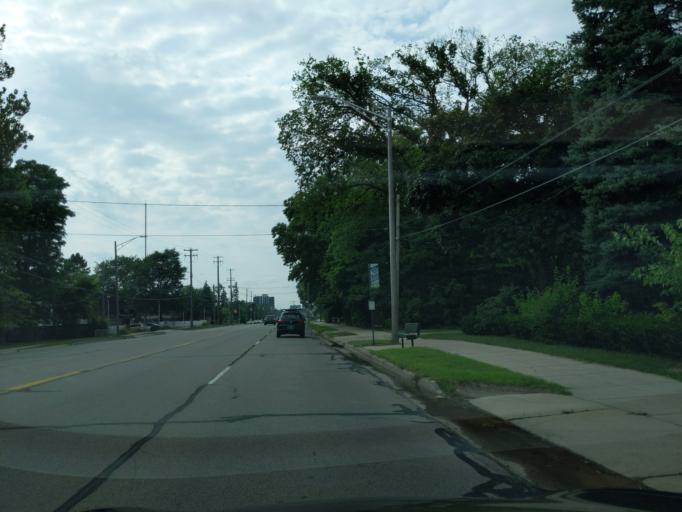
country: US
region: Michigan
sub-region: Ingham County
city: East Lansing
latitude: 42.7287
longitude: -84.4593
